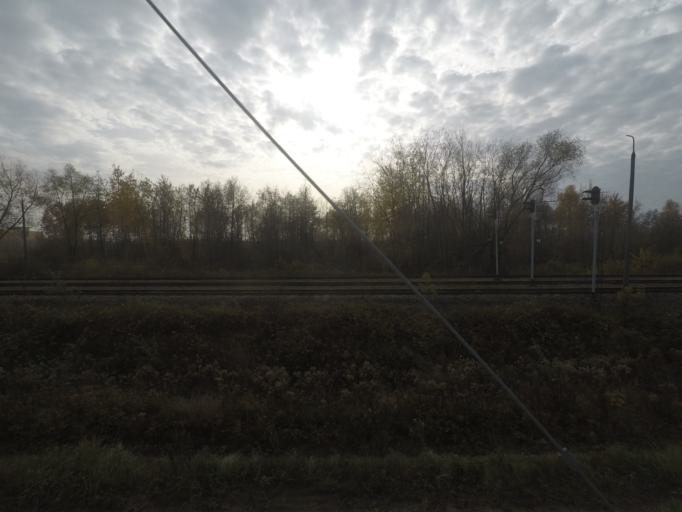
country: PL
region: Subcarpathian Voivodeship
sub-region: Powiat ropczycko-sedziszowski
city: Ostrow
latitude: 50.0793
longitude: 21.5930
